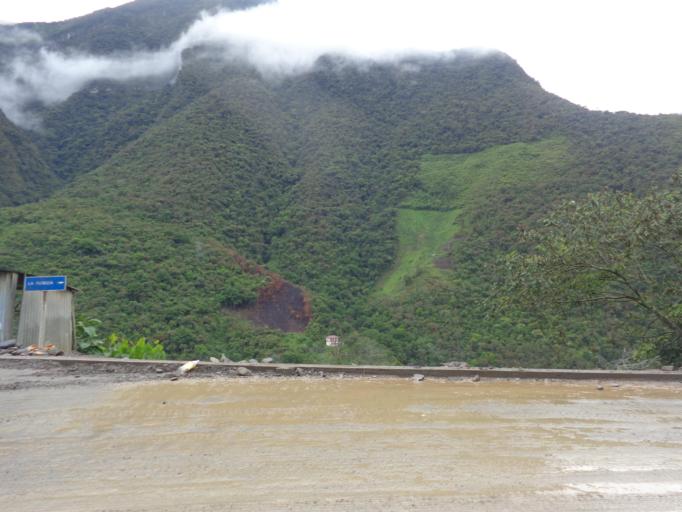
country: BO
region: La Paz
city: Coripata
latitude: -16.3638
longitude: -67.7525
